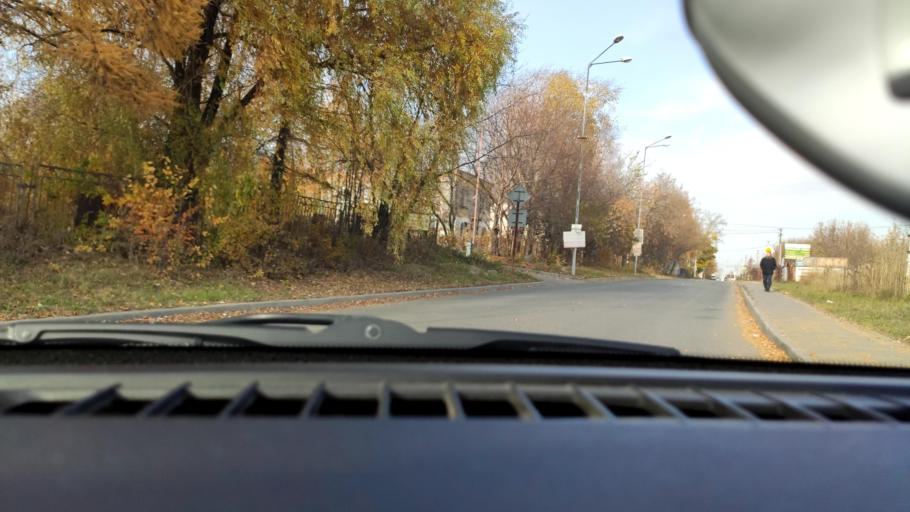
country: RU
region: Perm
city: Kondratovo
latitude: 57.9499
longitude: 56.1180
